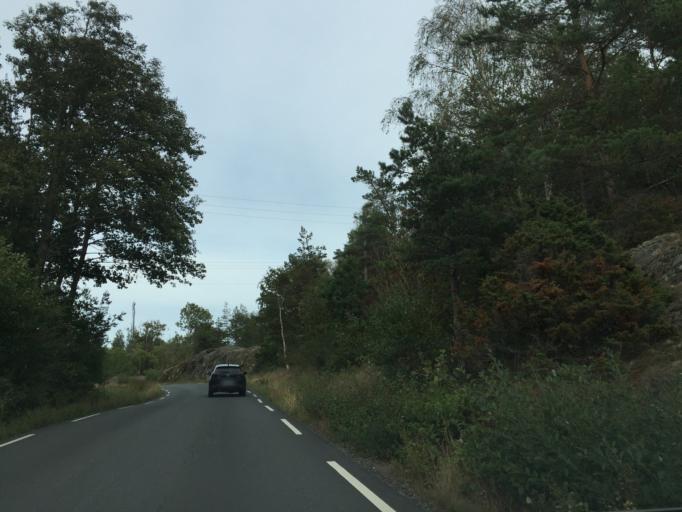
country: NO
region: Ostfold
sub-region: Hvaler
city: Skjaerhalden
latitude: 59.0405
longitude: 11.0293
